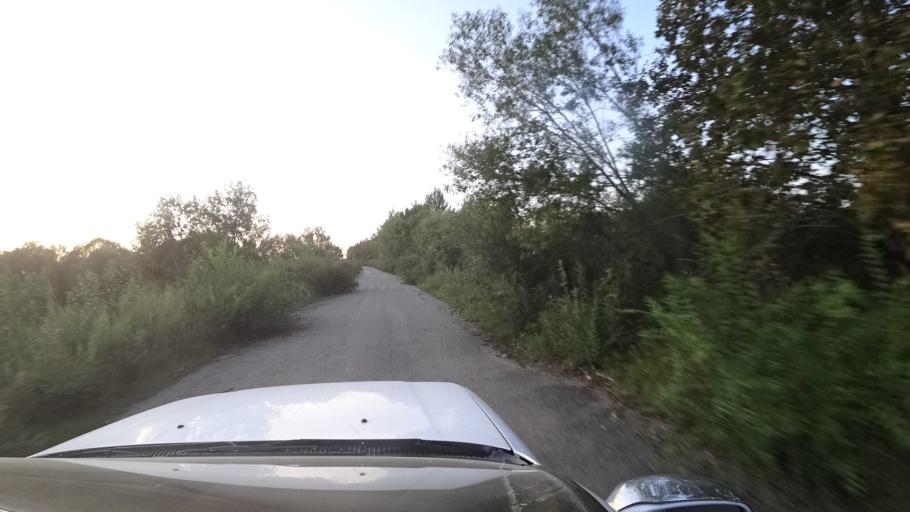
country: RU
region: Primorskiy
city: Dal'nerechensk
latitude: 45.9461
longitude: 133.7645
